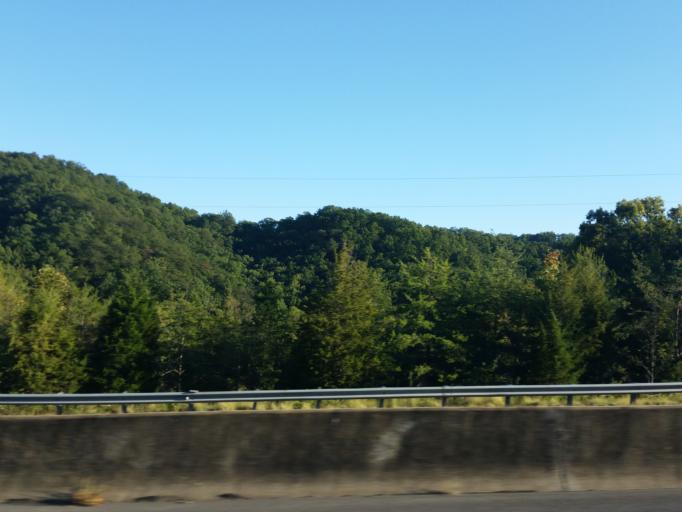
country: US
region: Tennessee
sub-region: Grainger County
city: Bean Station
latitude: 36.3578
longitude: -83.3577
